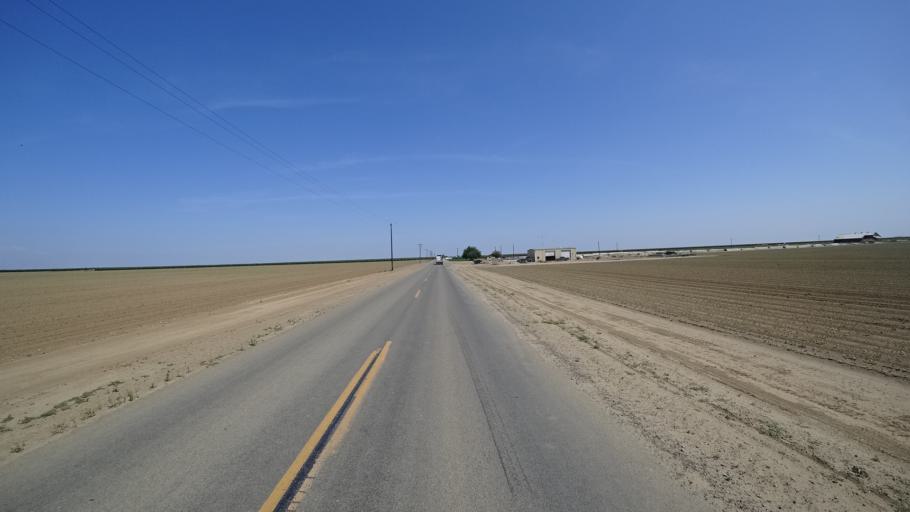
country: US
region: California
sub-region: Kings County
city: Kettleman City
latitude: 36.0734
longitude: -120.0034
